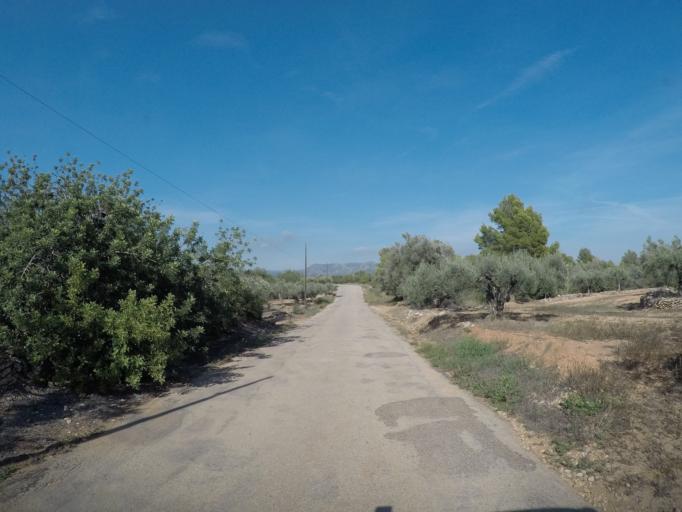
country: ES
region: Catalonia
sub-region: Provincia de Tarragona
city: El Perello
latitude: 40.8975
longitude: 0.7305
